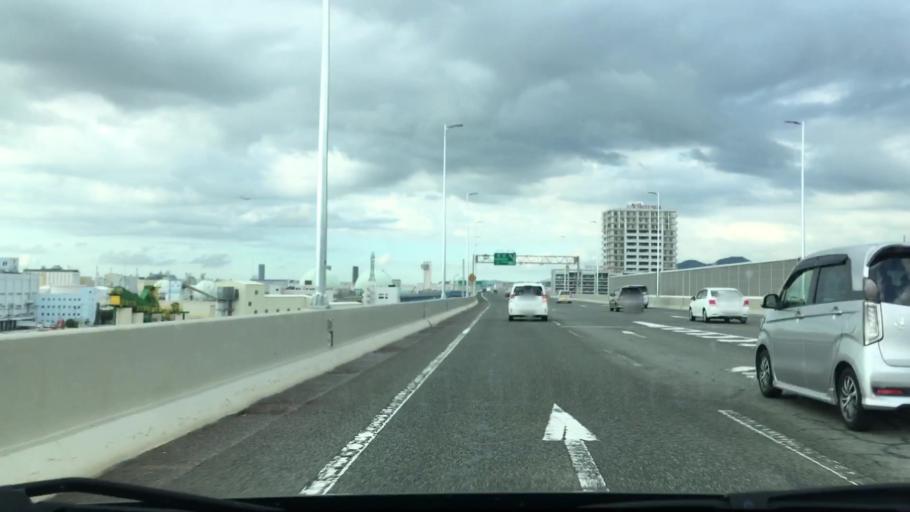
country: JP
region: Fukuoka
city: Fukuoka-shi
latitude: 33.6101
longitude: 130.4088
